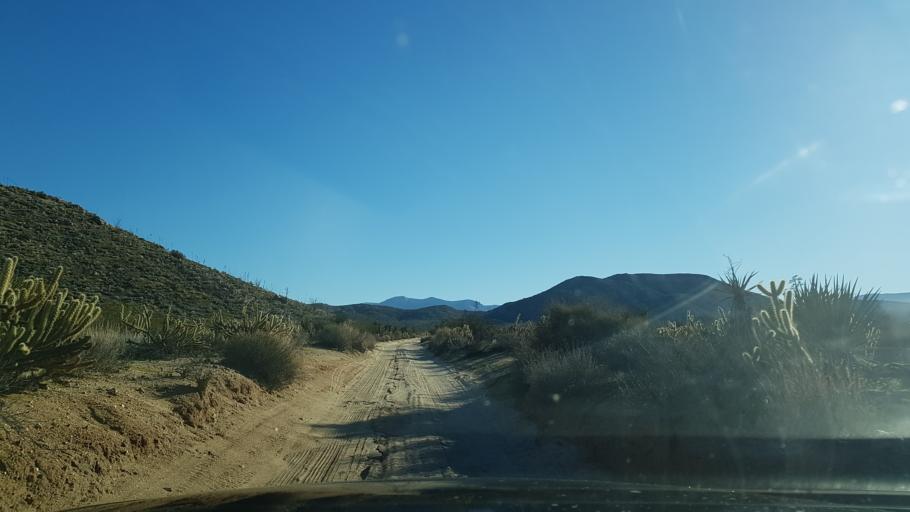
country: US
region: California
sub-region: San Diego County
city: Julian
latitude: 33.0162
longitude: -116.3962
